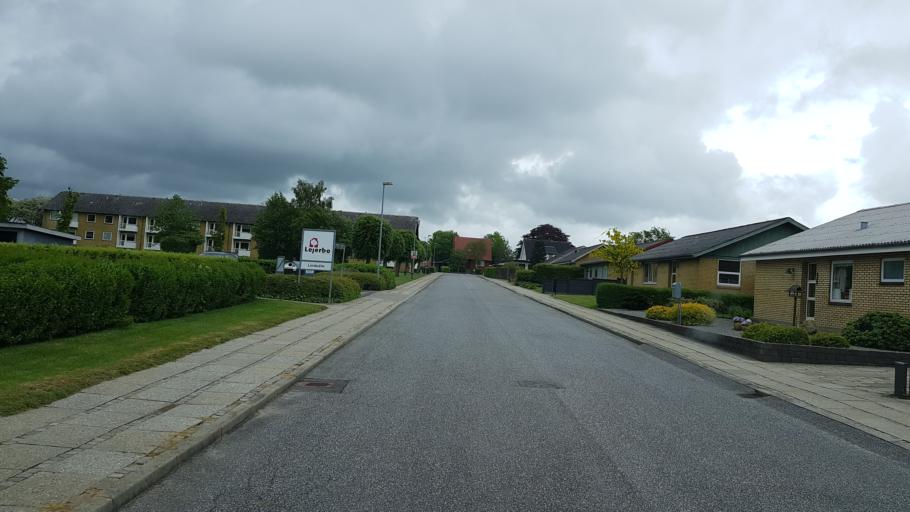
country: DK
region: Central Jutland
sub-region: Herning Kommune
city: Vildbjerg
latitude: 56.2007
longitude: 8.7616
